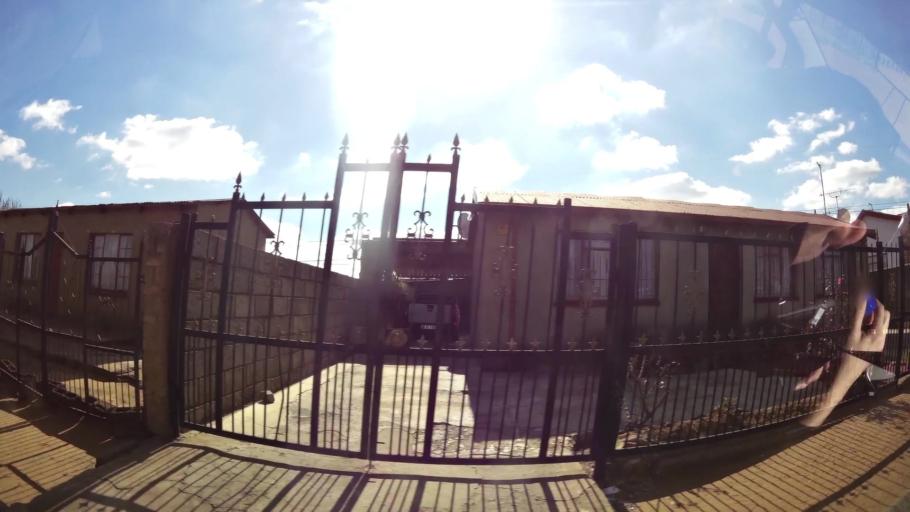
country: ZA
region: Gauteng
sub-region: West Rand District Municipality
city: Krugersdorp
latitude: -26.1424
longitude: 27.7942
